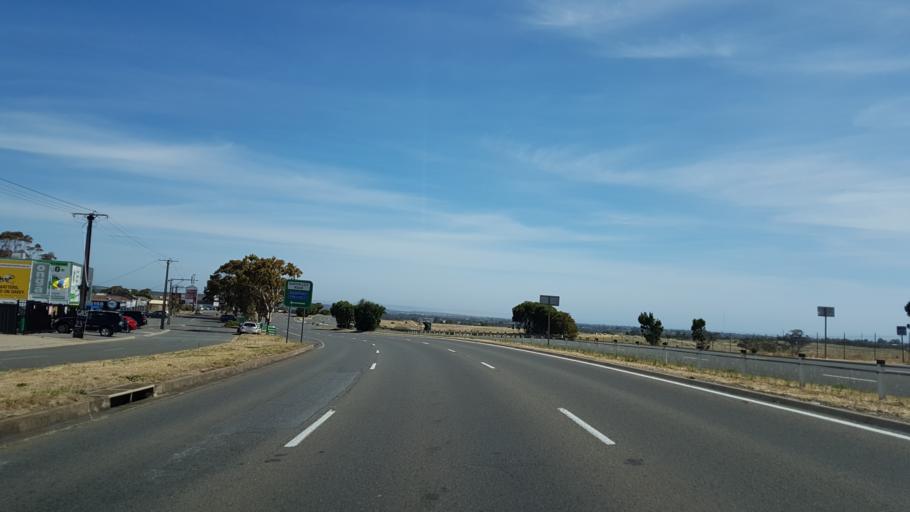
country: AU
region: South Australia
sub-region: Marion
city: Trott Park
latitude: -35.0645
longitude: 138.5551
